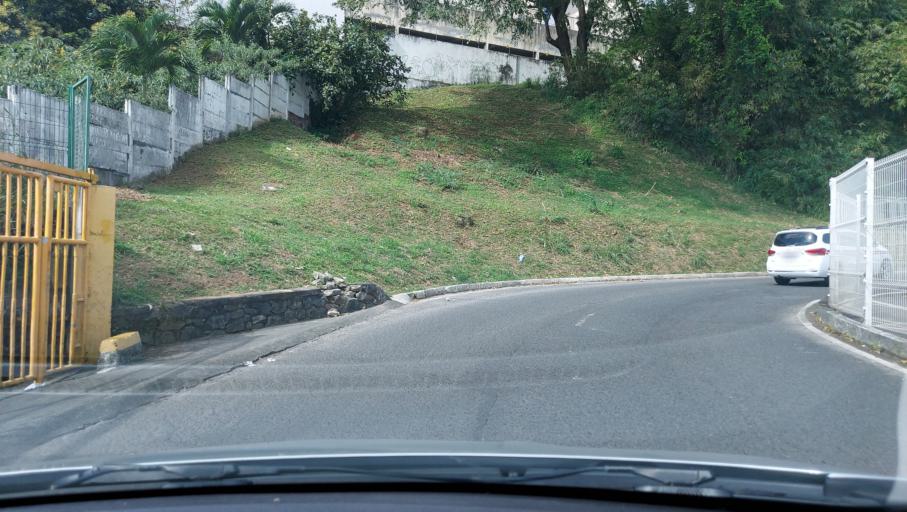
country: BR
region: Bahia
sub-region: Salvador
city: Salvador
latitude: -12.9815
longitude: -38.4621
